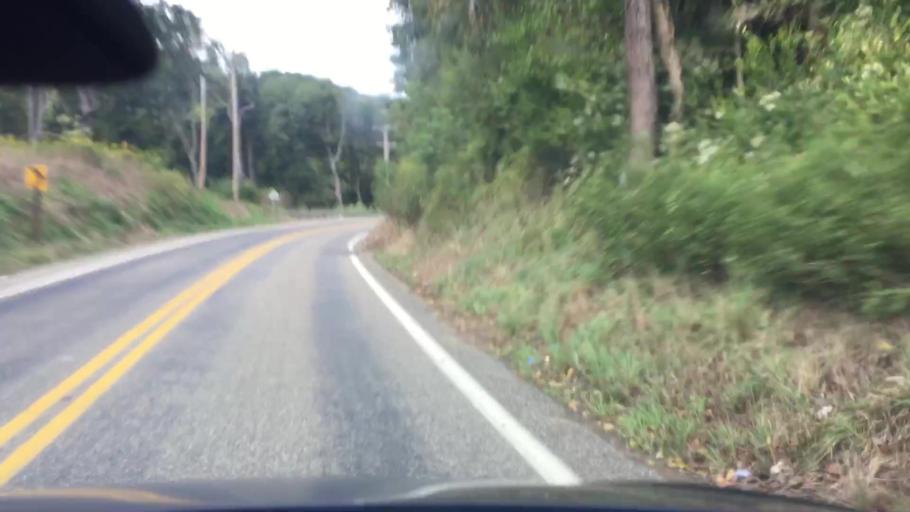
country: US
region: Pennsylvania
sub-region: Allegheny County
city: Cheswick
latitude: 40.5649
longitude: -79.8205
